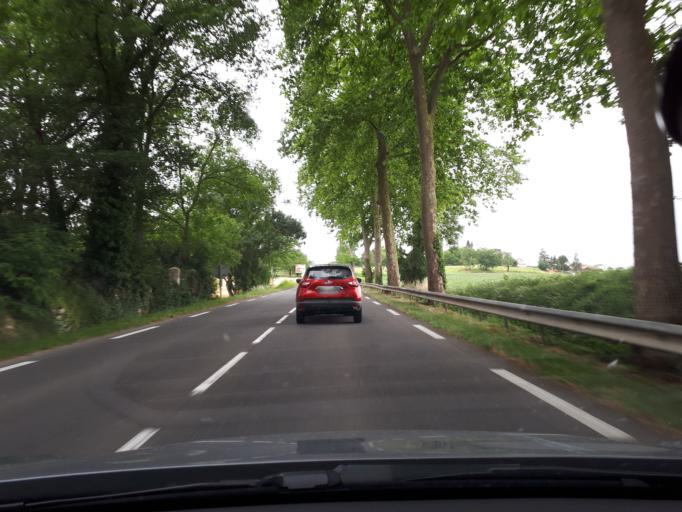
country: FR
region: Midi-Pyrenees
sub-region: Departement du Gers
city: Lectoure
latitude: 43.9385
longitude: 0.6501
